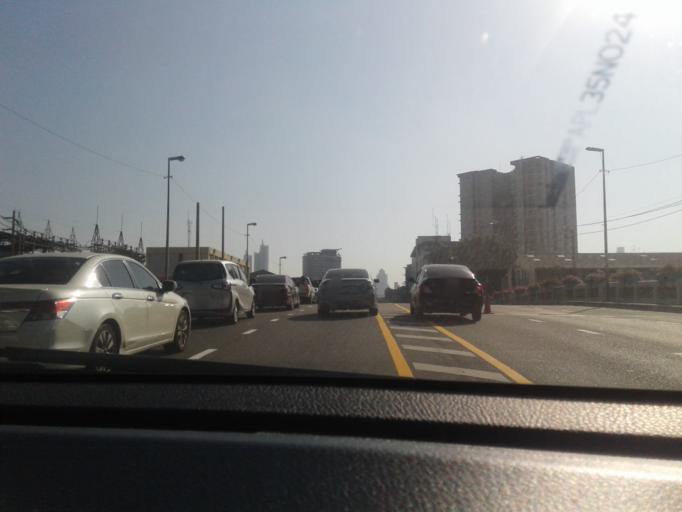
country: TH
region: Bangkok
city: Thon Buri
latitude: 13.7276
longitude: 100.4850
